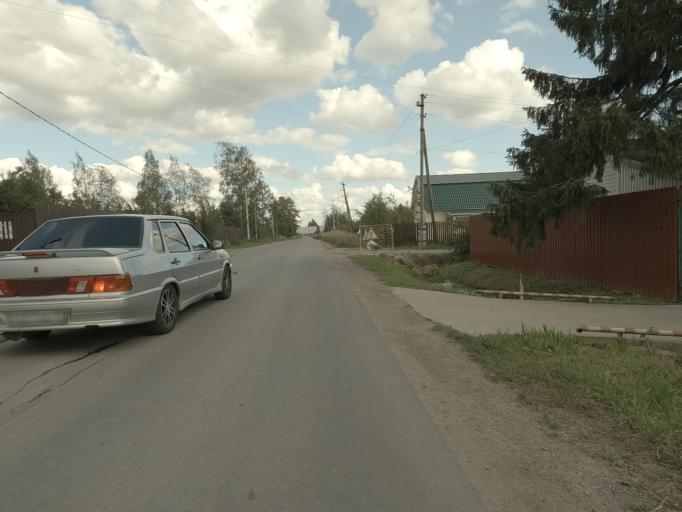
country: RU
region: Leningrad
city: Ul'yanovka
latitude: 59.6327
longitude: 30.7817
